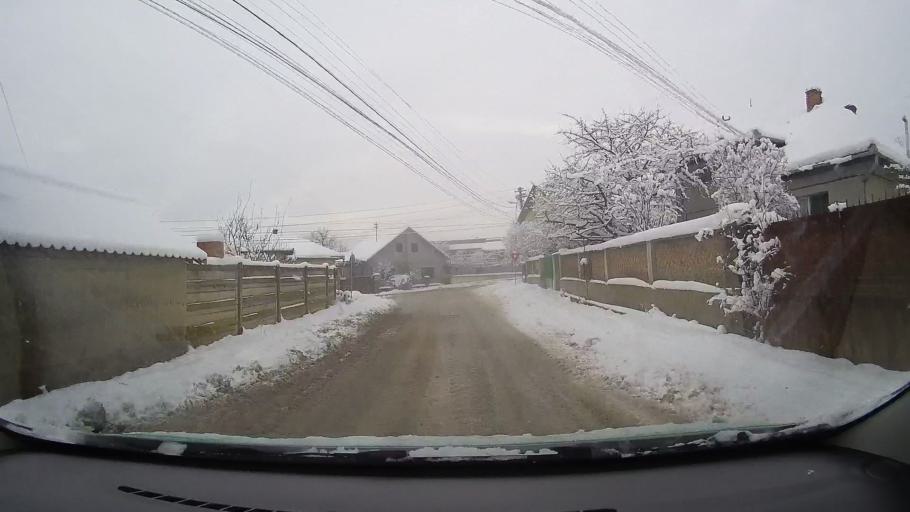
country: RO
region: Alba
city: Vurpar
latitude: 45.9787
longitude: 23.4820
